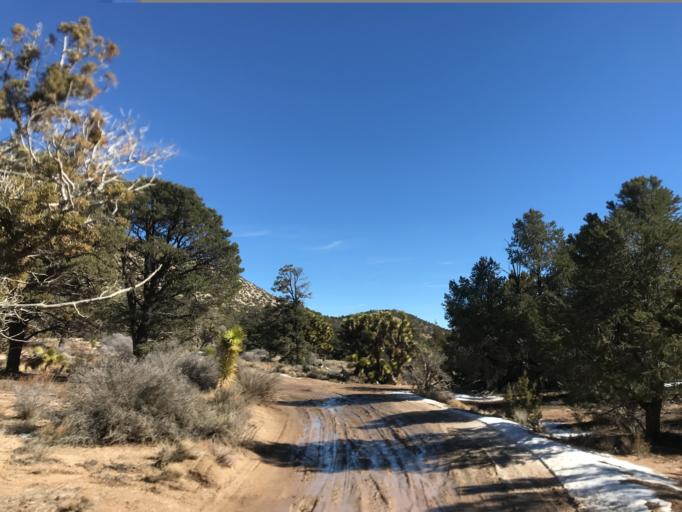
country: US
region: California
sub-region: San Bernardino County
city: Big Bear City
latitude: 34.2417
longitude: -116.6969
